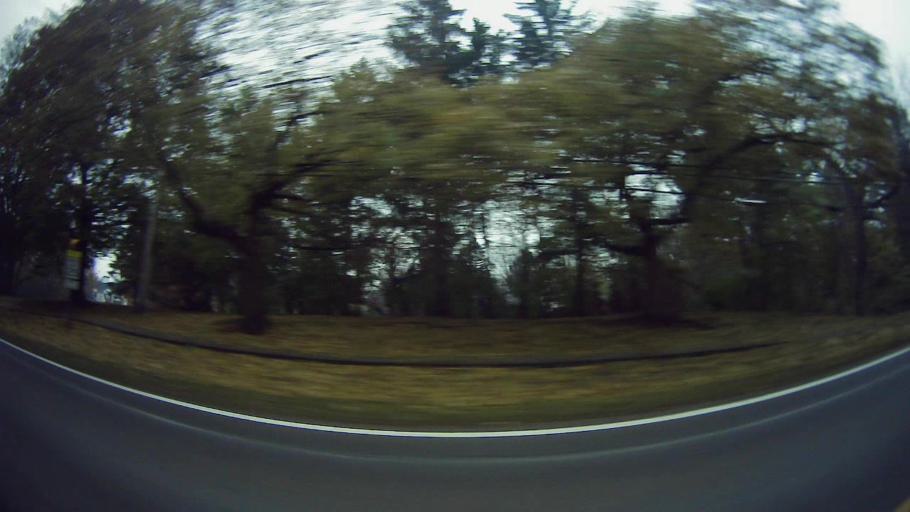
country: US
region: Michigan
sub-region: Oakland County
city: Bloomfield Hills
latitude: 42.5595
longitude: -83.2526
